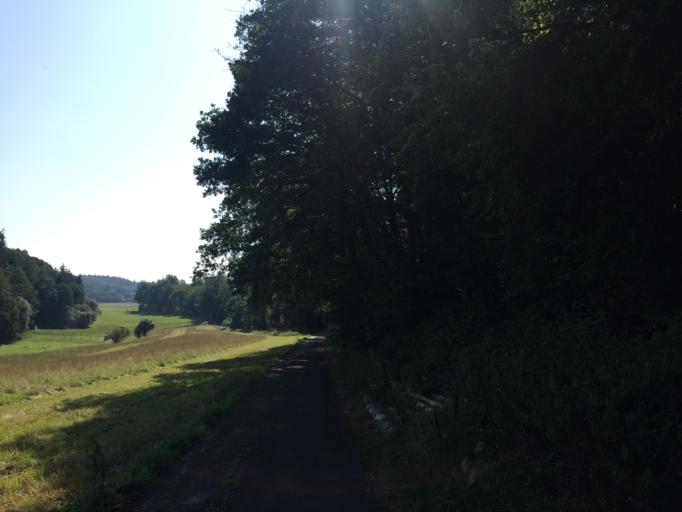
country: DE
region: Hesse
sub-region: Regierungsbezirk Darmstadt
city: Butzbach
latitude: 50.4353
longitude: 8.5886
